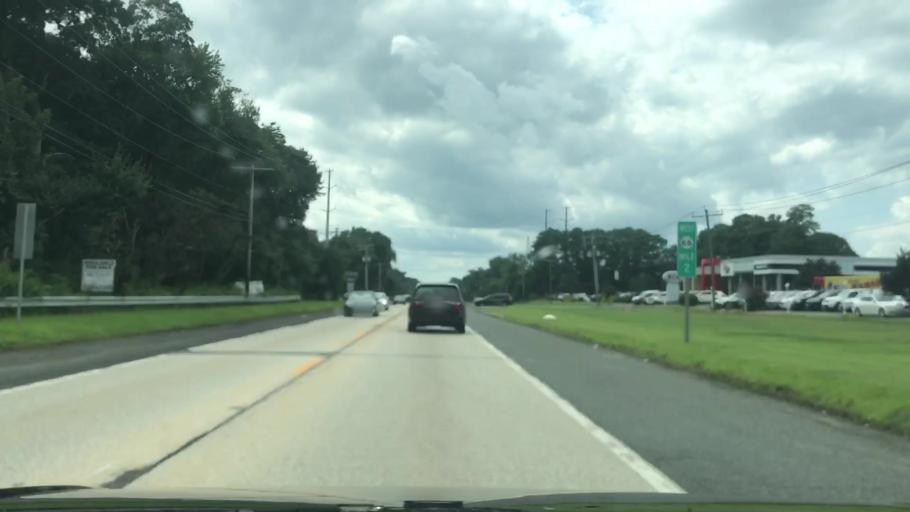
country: US
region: New Jersey
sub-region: Monmouth County
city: Shark River Hills
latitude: 40.2282
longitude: -74.0680
